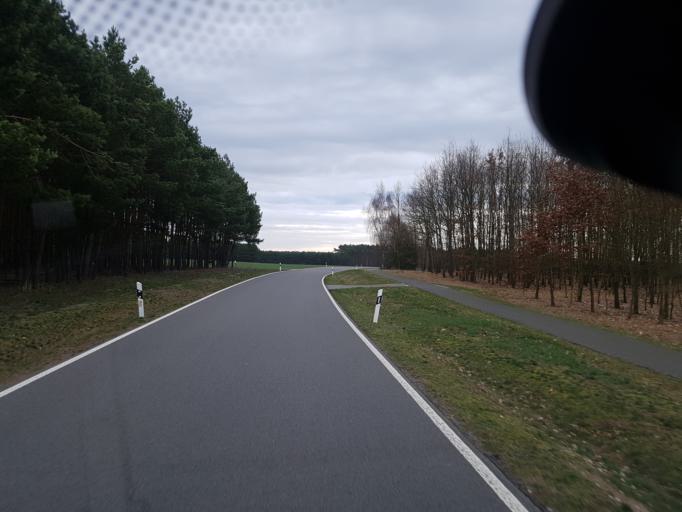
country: DE
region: Brandenburg
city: Mixdorf
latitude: 52.2028
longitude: 14.3671
